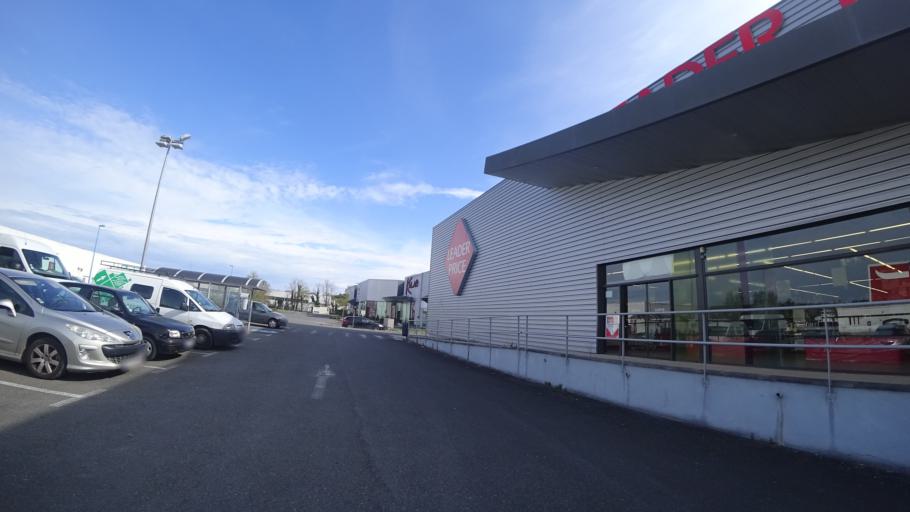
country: FR
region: Midi-Pyrenees
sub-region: Departement de l'Aveyron
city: Sebazac-Concoures
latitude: 44.3756
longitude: 2.5941
